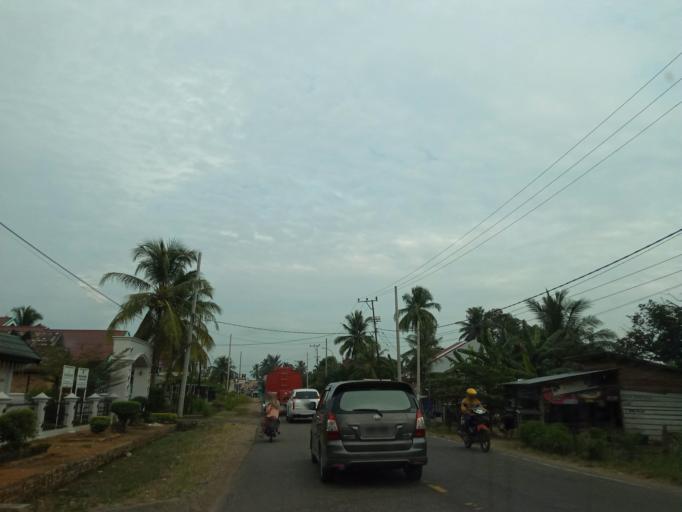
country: ID
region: Jambi
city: Muara Tembesi
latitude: -1.7213
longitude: 103.1279
